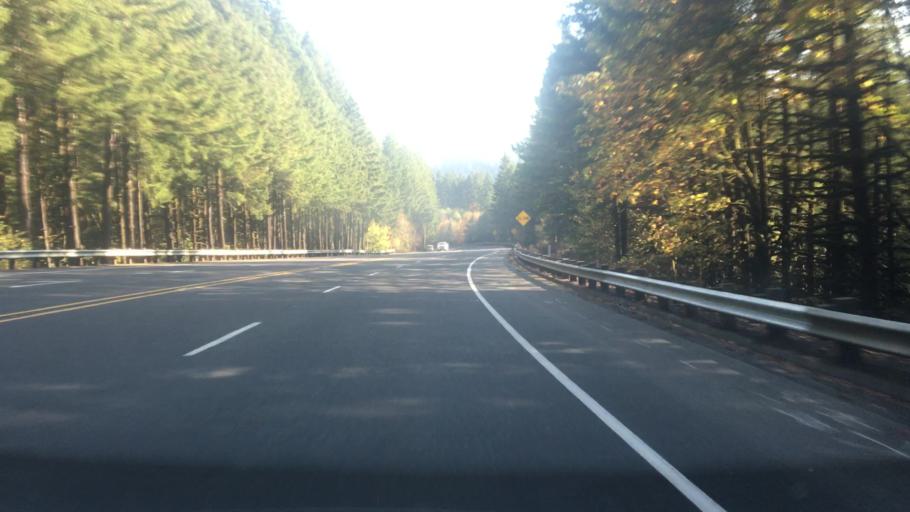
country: US
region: Oregon
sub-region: Polk County
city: Grand Ronde
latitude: 45.0603
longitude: -123.6887
